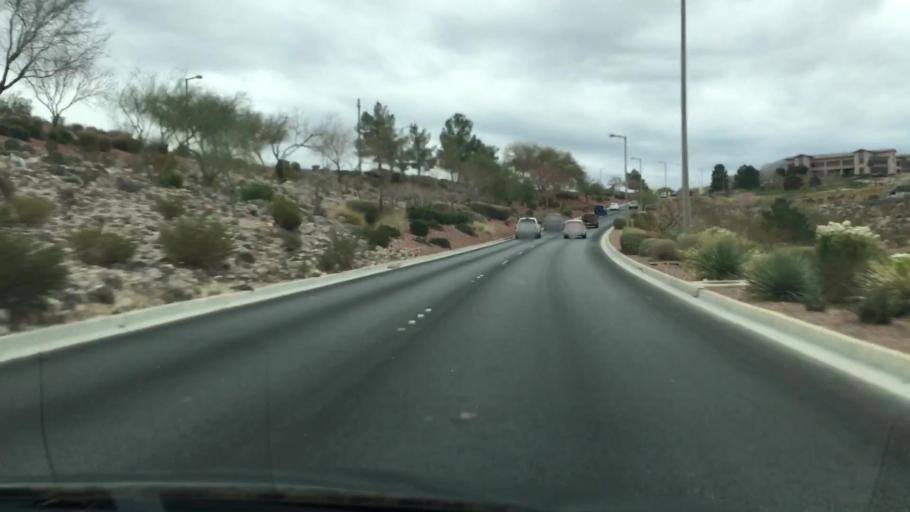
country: US
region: Nevada
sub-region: Clark County
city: Whitney
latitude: 35.9609
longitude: -115.0958
